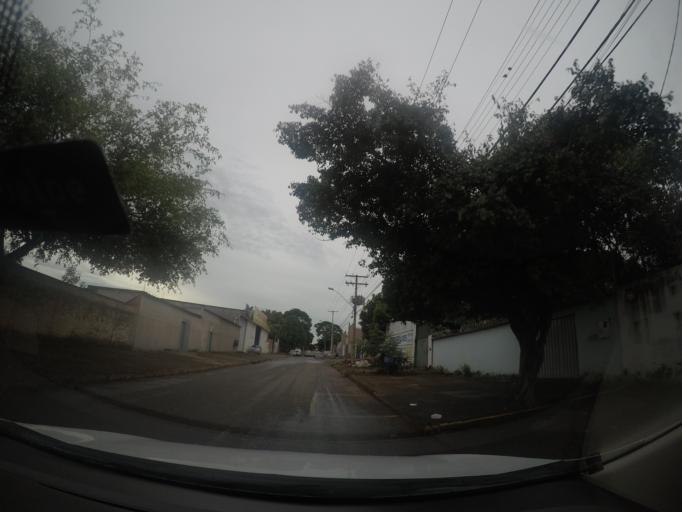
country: BR
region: Goias
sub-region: Goiania
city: Goiania
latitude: -16.6283
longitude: -49.2344
